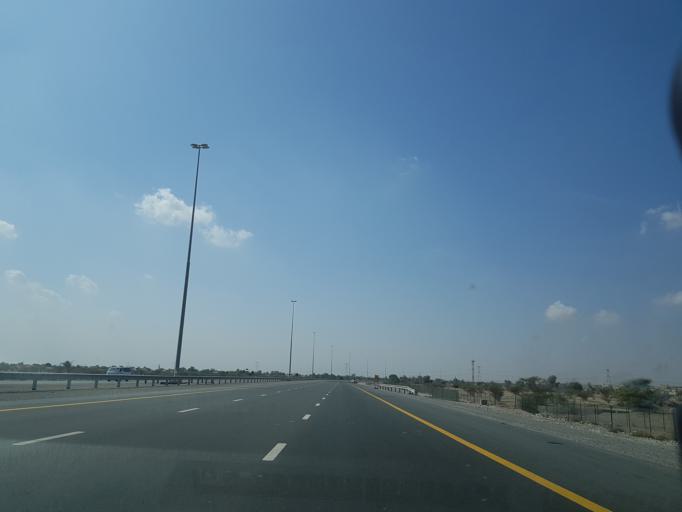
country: AE
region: Ra's al Khaymah
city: Ras al-Khaimah
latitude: 25.7048
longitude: 55.9947
